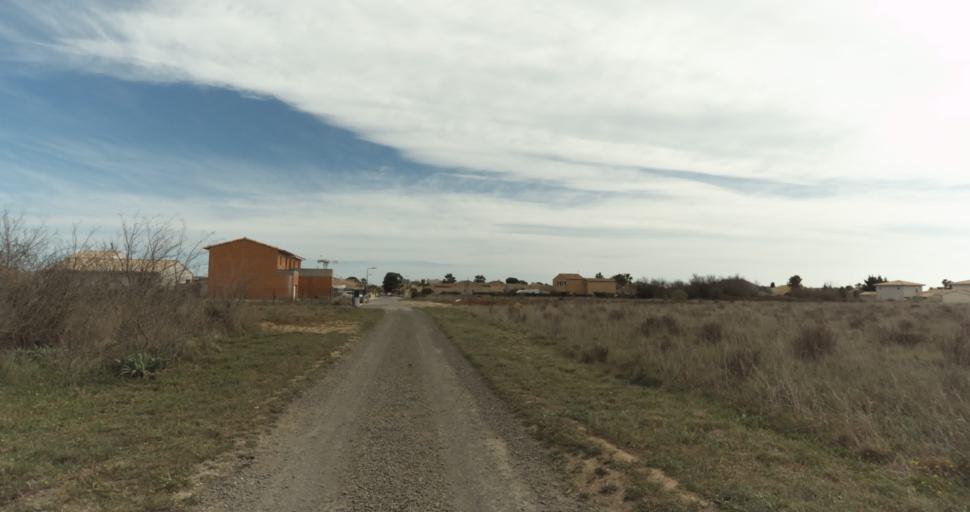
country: FR
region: Languedoc-Roussillon
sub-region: Departement de l'Herault
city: Marseillan
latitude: 43.3394
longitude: 3.5289
